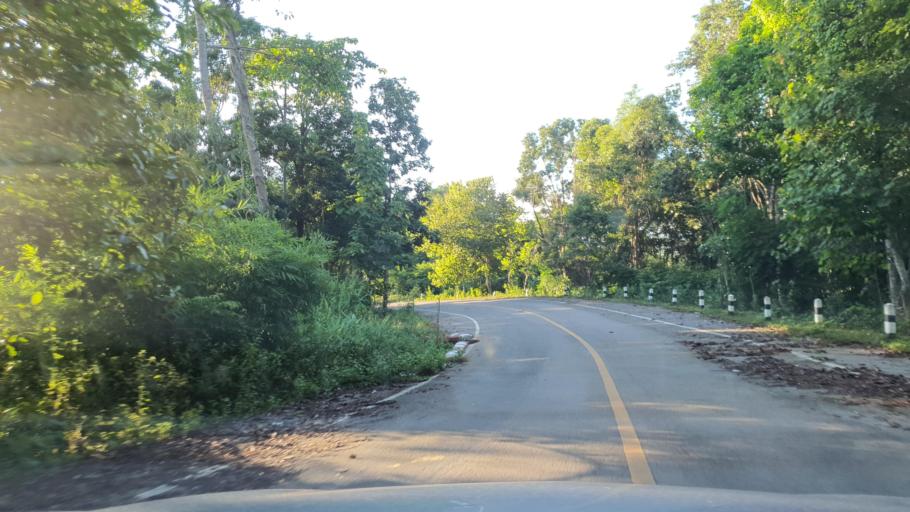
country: TH
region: Chiang Mai
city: Mae On
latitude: 18.8071
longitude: 99.3038
